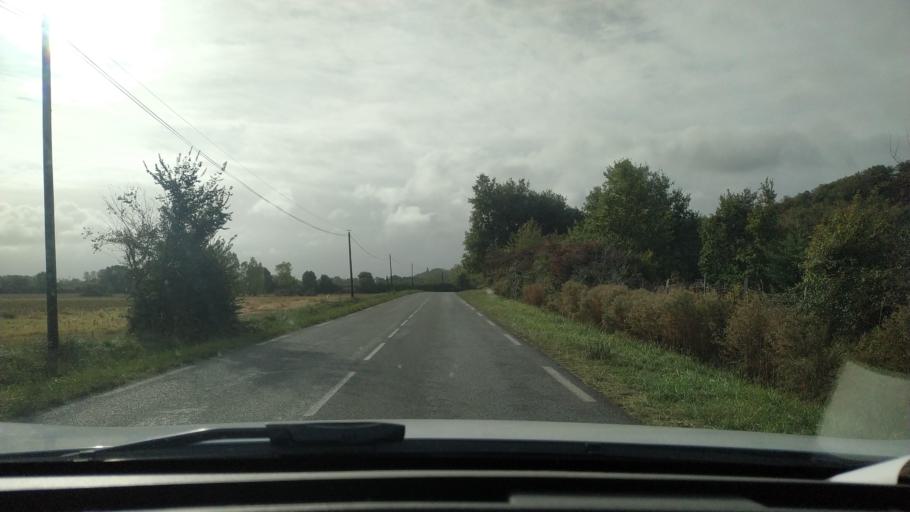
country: FR
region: Midi-Pyrenees
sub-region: Departement de la Haute-Garonne
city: Auterive
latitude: 43.3228
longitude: 1.4463
